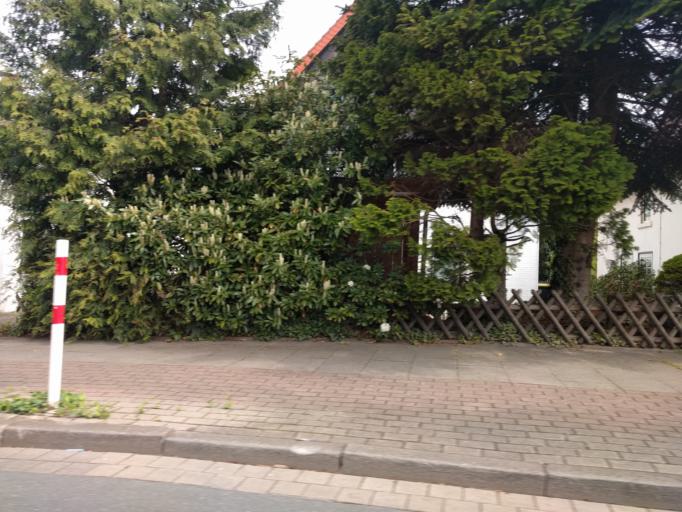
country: DE
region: North Rhine-Westphalia
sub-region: Regierungsbezirk Detmold
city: Bielefeld
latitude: 52.0570
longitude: 8.5536
